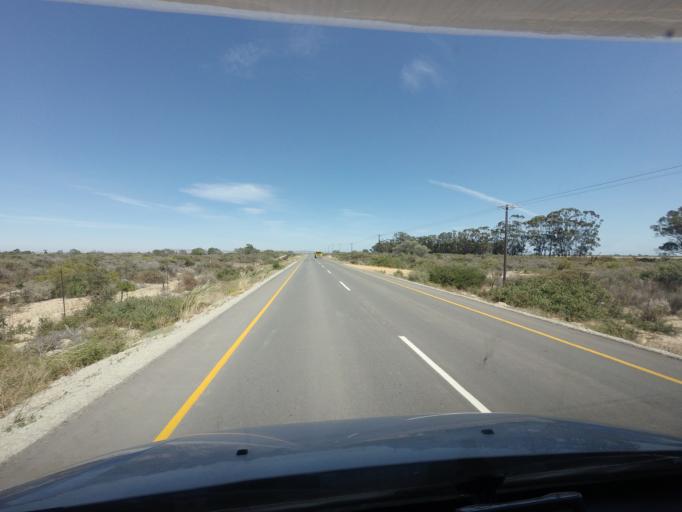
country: ZA
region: Western Cape
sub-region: West Coast District Municipality
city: Vredenburg
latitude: -32.7945
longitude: 18.2416
